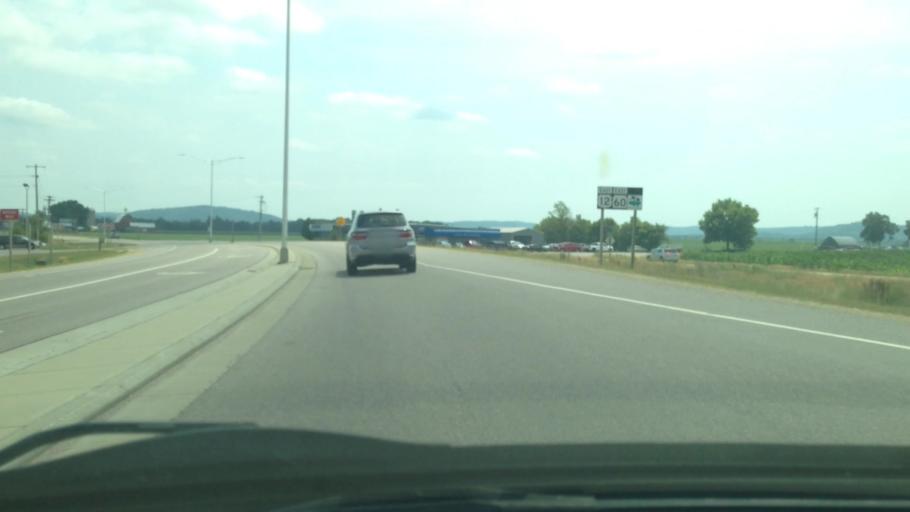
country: US
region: Wisconsin
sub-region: Sauk County
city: Sauk City
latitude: 43.2712
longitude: -89.7560
